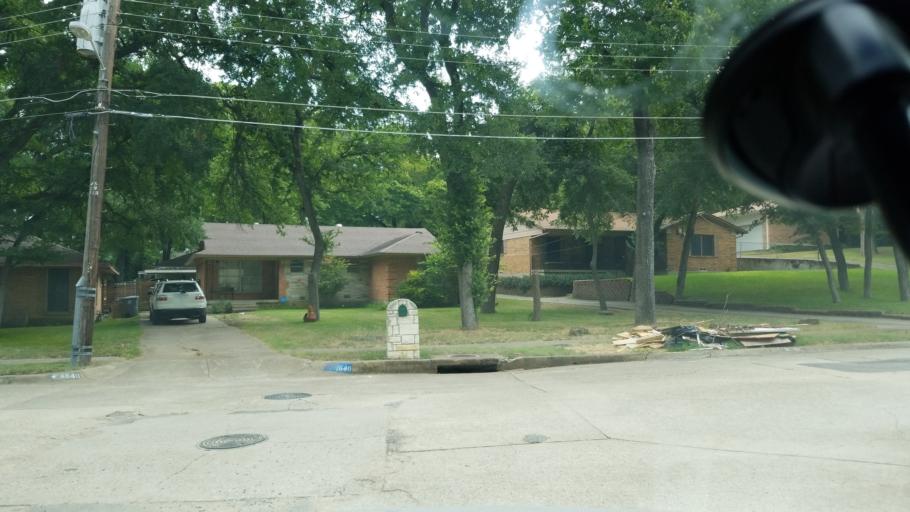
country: US
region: Texas
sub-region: Dallas County
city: Cockrell Hill
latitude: 32.6877
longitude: -96.8497
